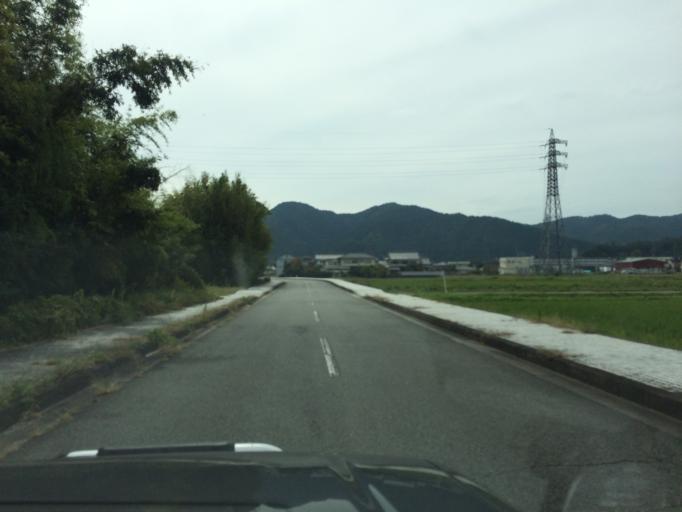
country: JP
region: Hyogo
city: Sasayama
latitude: 35.0726
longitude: 135.2135
